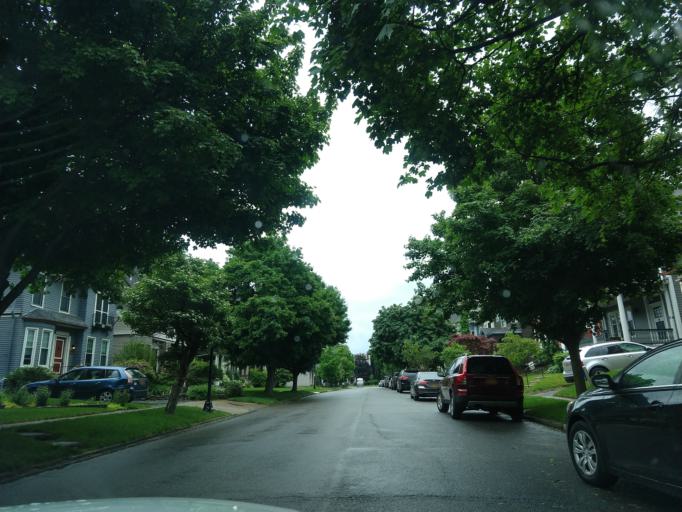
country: US
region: New York
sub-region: Erie County
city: Buffalo
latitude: 42.9184
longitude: -78.8707
